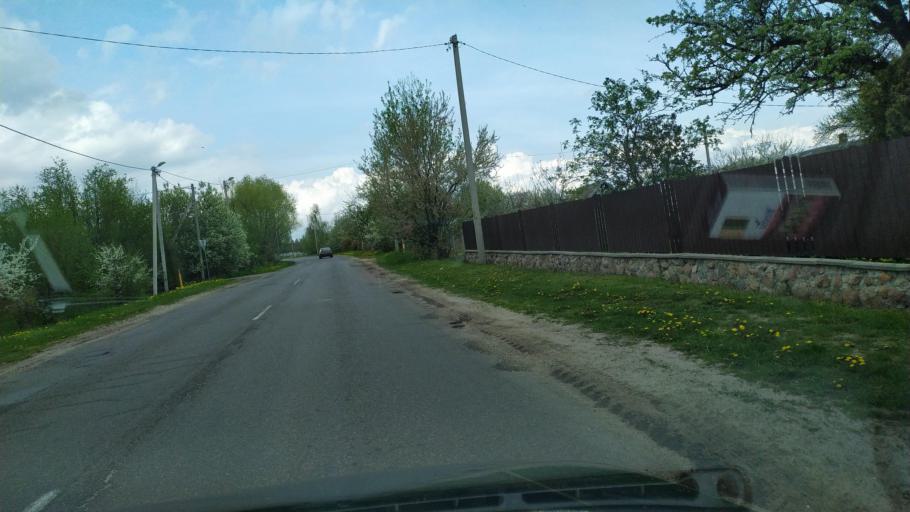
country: BY
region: Brest
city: Pruzhany
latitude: 52.5861
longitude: 24.4110
